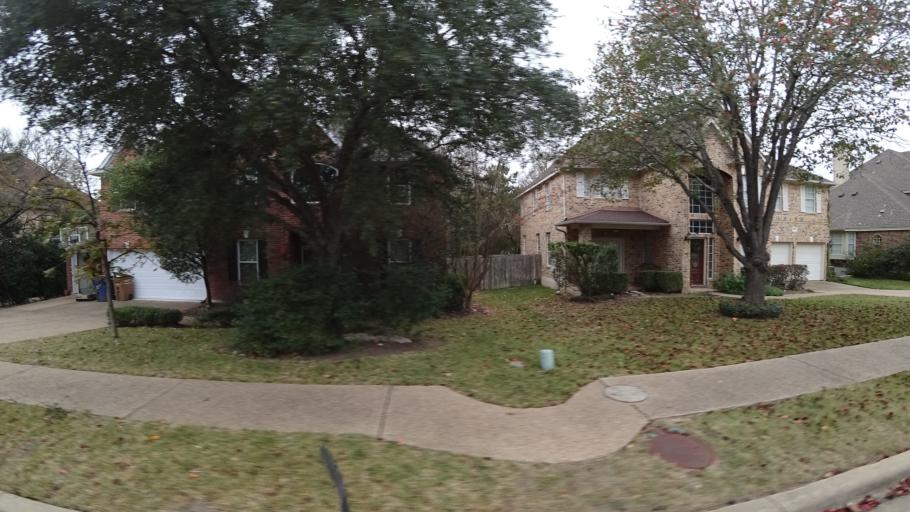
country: US
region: Texas
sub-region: Williamson County
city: Jollyville
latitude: 30.3929
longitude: -97.8017
